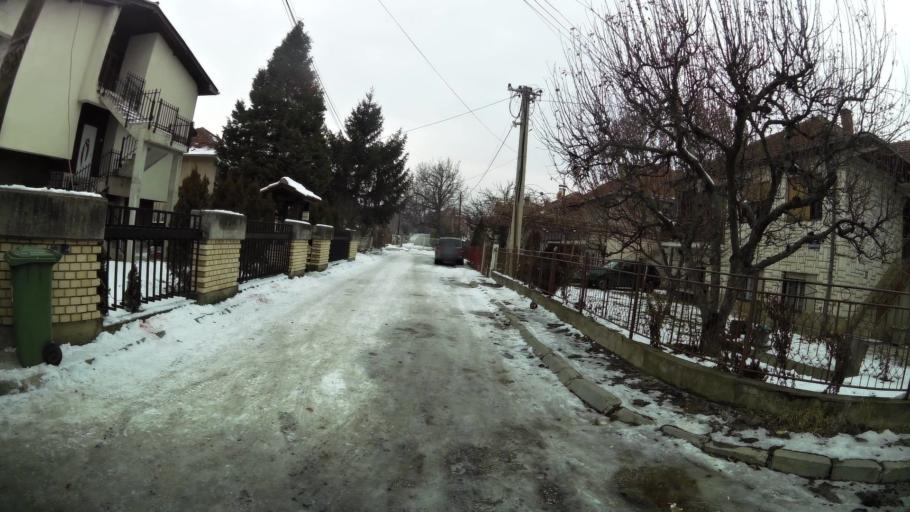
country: MK
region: Butel
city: Butel
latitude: 42.0373
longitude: 21.4446
